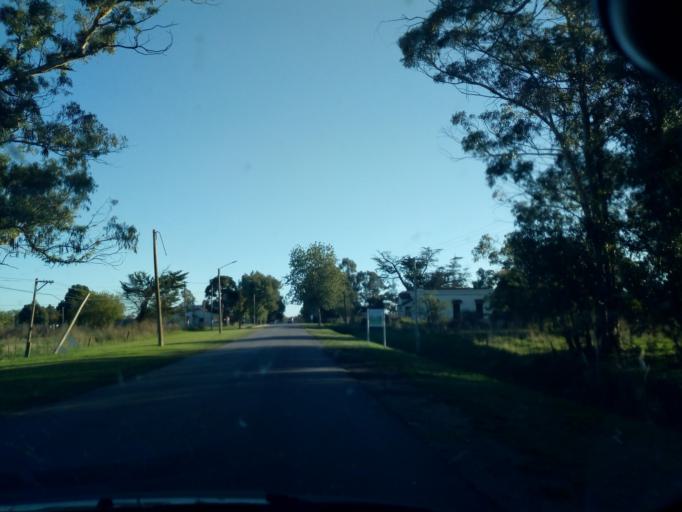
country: AR
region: Buenos Aires
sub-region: Partido de Loberia
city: Loberia
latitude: -38.1523
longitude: -58.7692
